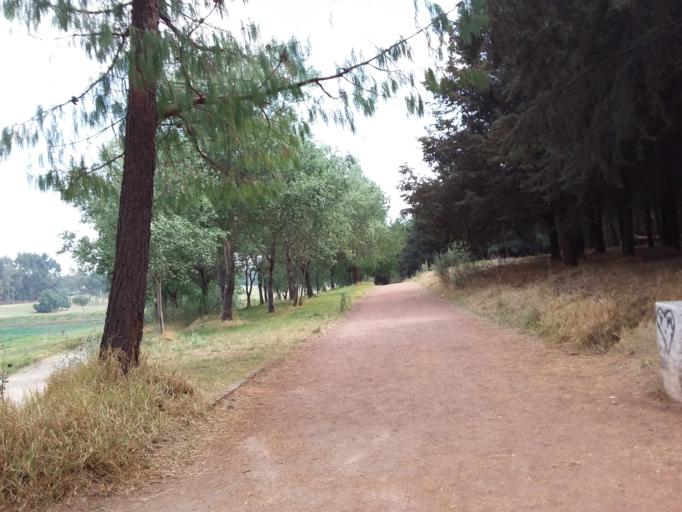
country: MX
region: Mexico
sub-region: Toluca
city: San Antonio Buenavista
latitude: 19.2739
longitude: -99.6971
